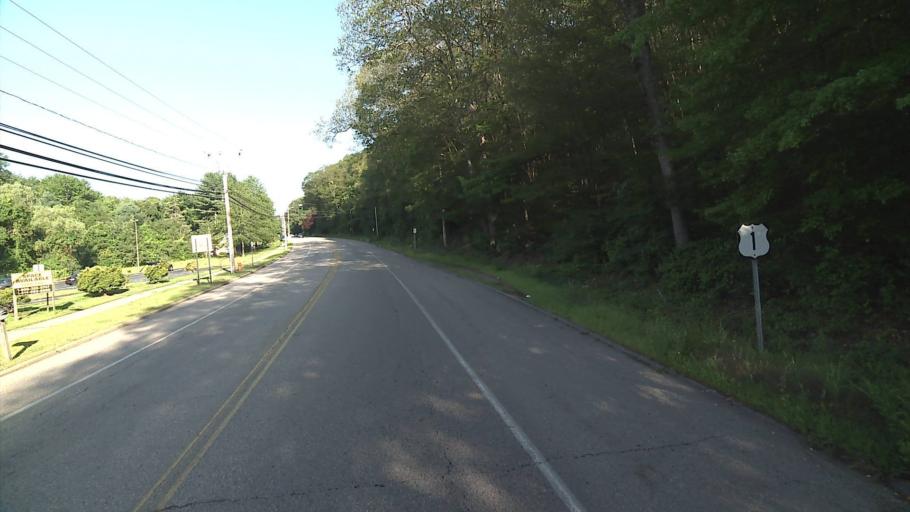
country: US
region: Connecticut
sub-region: New London County
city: Central Waterford
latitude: 41.3505
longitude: -72.1530
